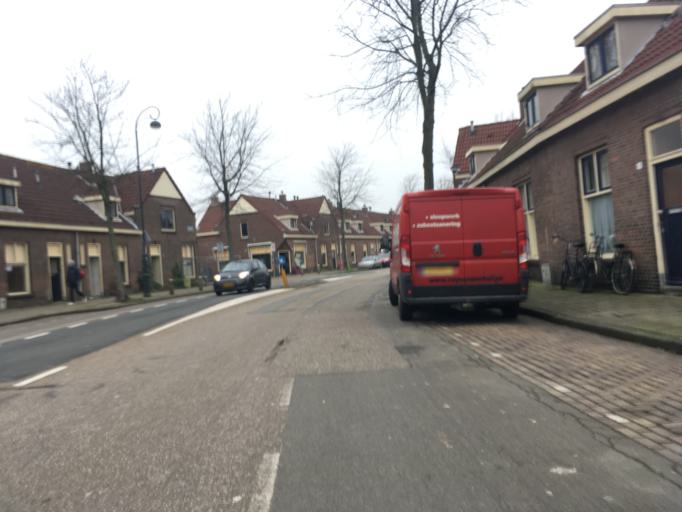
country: NL
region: North Holland
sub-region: Gemeente Haarlem
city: Haarlem
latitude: 52.3744
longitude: 4.6488
